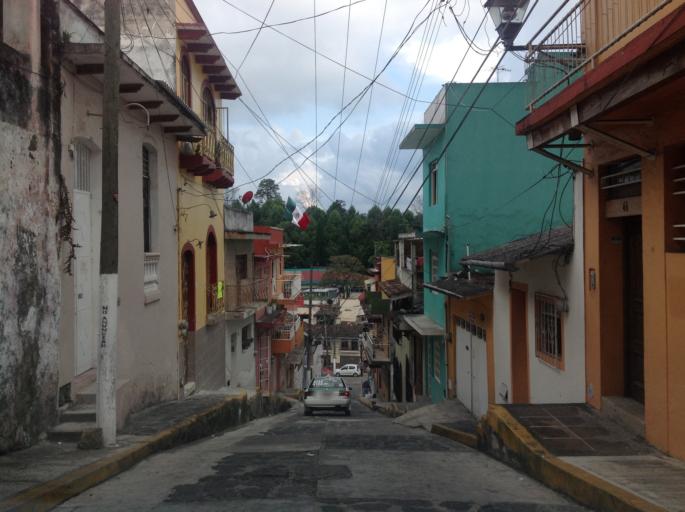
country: MX
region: Veracruz
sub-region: Xalapa
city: Xalapa de Enriquez
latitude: 19.5249
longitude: -96.9214
